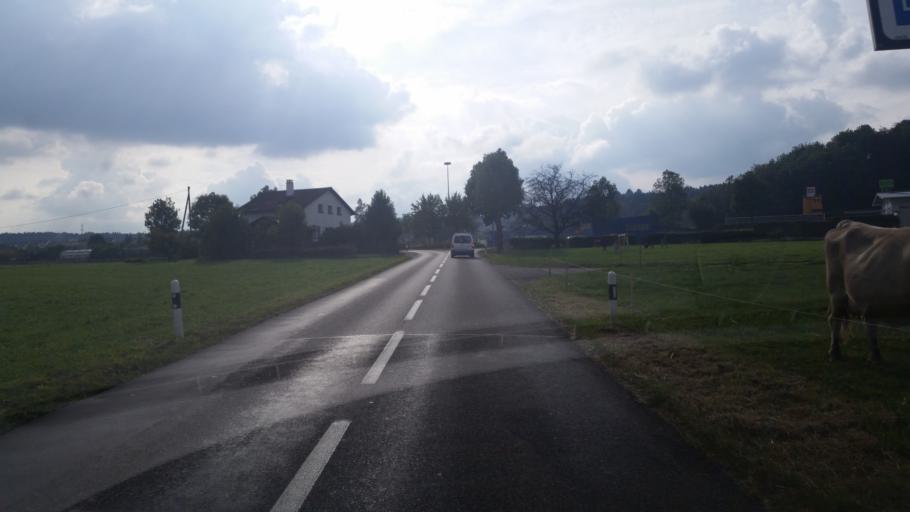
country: CH
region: Aargau
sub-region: Bezirk Baden
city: Kunten
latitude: 47.3845
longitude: 8.2994
